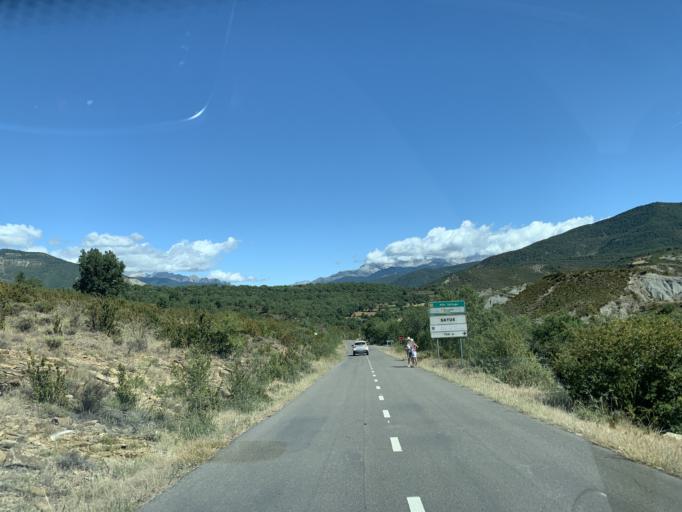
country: ES
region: Aragon
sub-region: Provincia de Huesca
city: Sabinanigo
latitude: 42.5309
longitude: -0.3238
